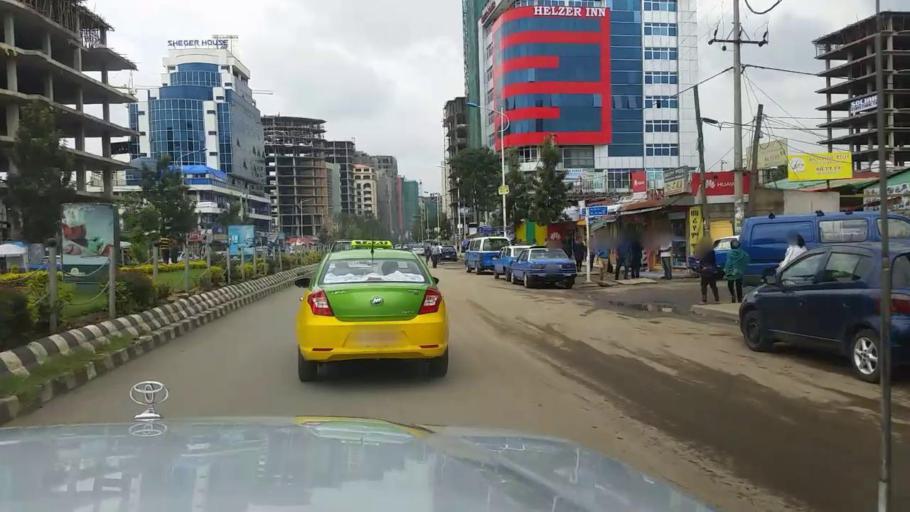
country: ET
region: Adis Abeba
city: Addis Ababa
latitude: 8.9983
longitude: 38.7864
